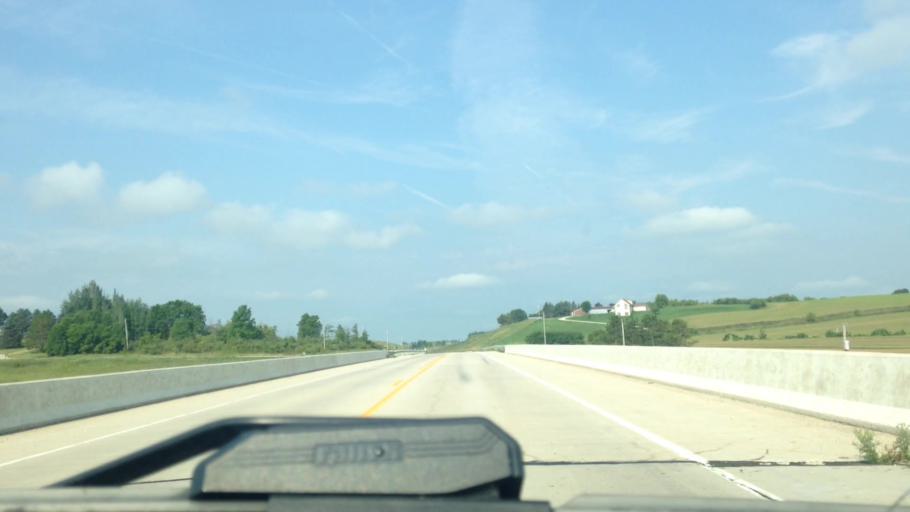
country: US
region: Wisconsin
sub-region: Dodge County
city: Theresa
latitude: 43.5365
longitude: -88.4322
